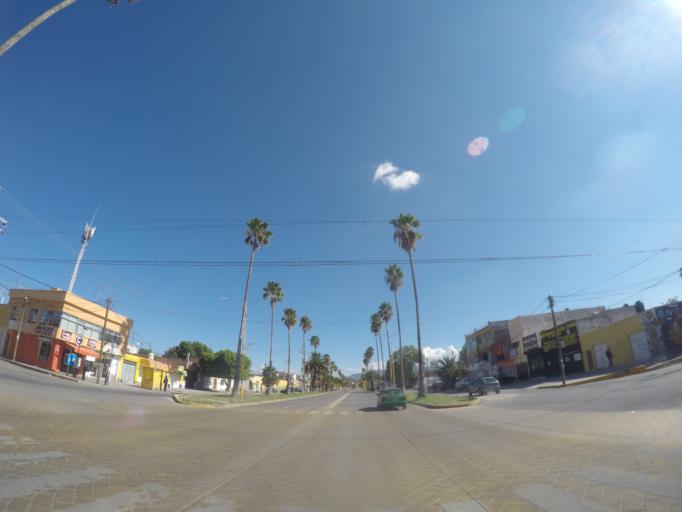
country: MX
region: San Luis Potosi
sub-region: San Luis Potosi
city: San Luis Potosi
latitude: 22.1665
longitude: -100.9724
